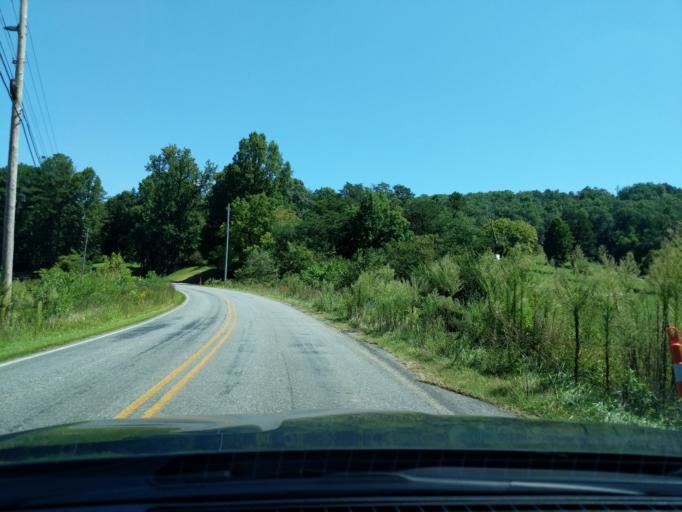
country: US
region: Georgia
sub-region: Towns County
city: Hiawassee
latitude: 35.0099
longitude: -83.7429
